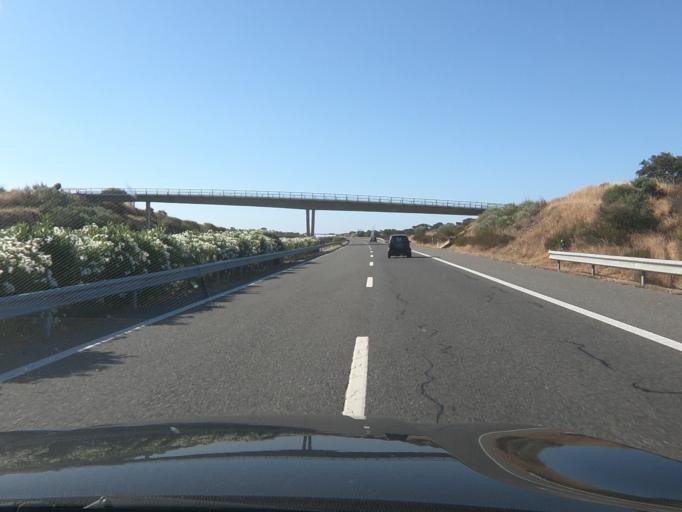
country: PT
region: Beja
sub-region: Ourique
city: Ourique
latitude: 37.5515
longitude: -8.1910
